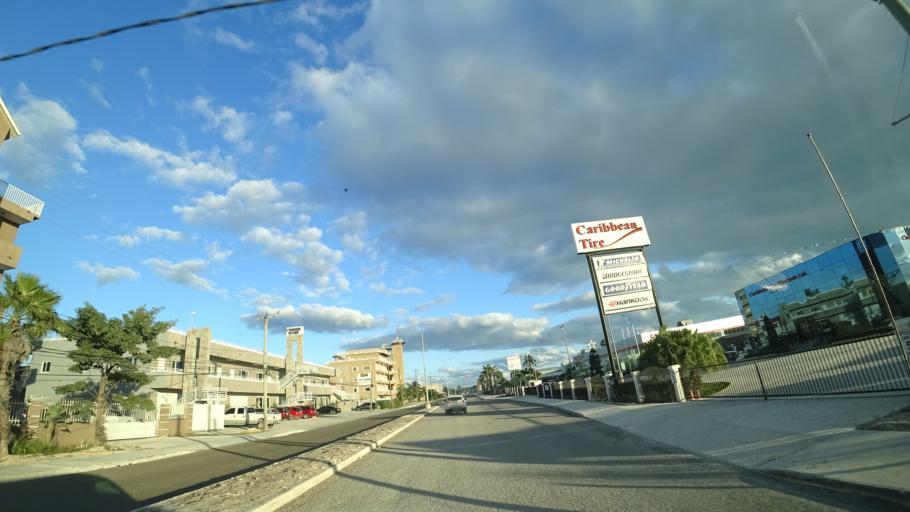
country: BZ
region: Belize
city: Belize City
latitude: 17.5154
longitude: -88.2258
